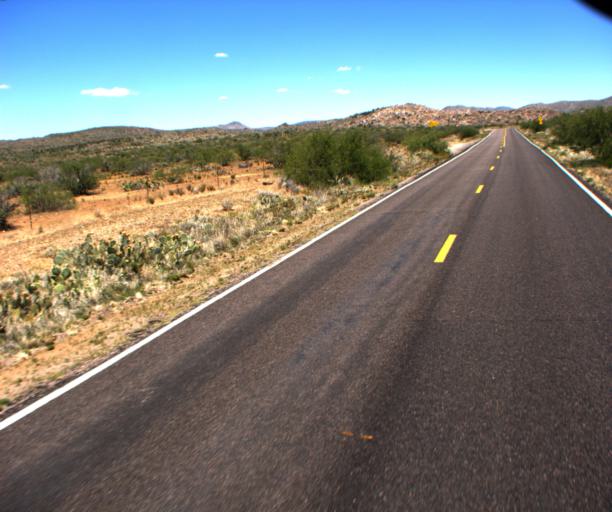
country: US
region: Arizona
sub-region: Yavapai County
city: Bagdad
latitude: 34.5150
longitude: -113.1480
